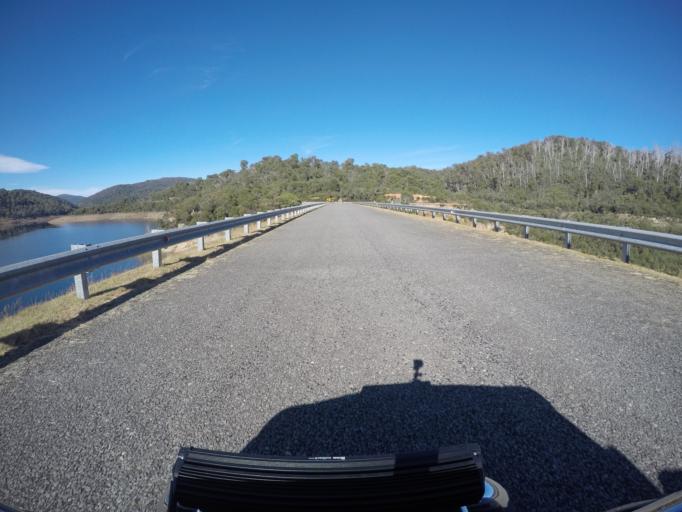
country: AU
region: New South Wales
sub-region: Snowy River
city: Jindabyne
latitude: -36.0507
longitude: 148.2756
